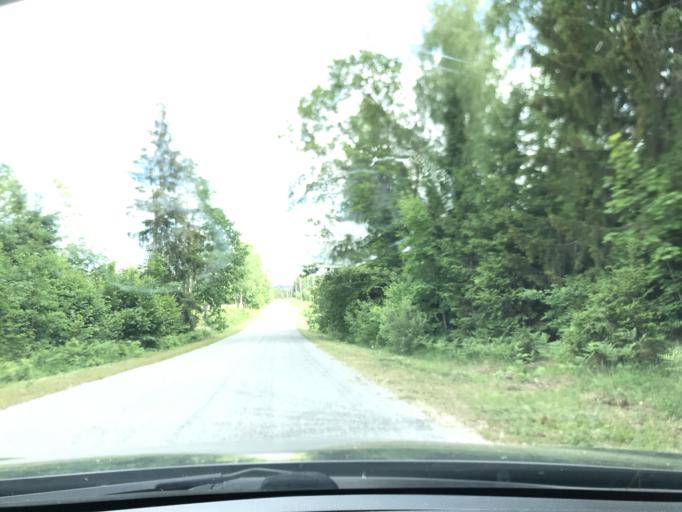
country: LV
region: Alsunga
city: Alsunga
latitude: 56.9924
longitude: 21.6251
